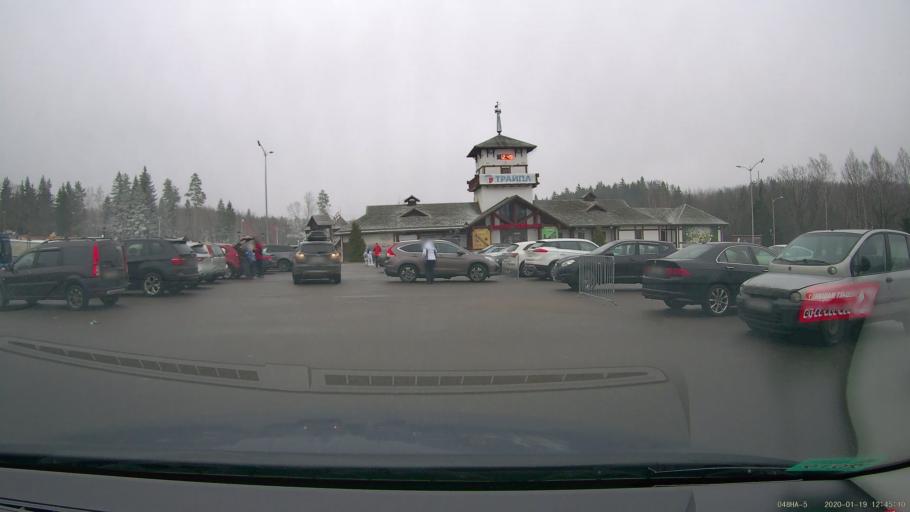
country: BY
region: Minsk
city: Lahoysk
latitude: 54.1826
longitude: 27.8091
